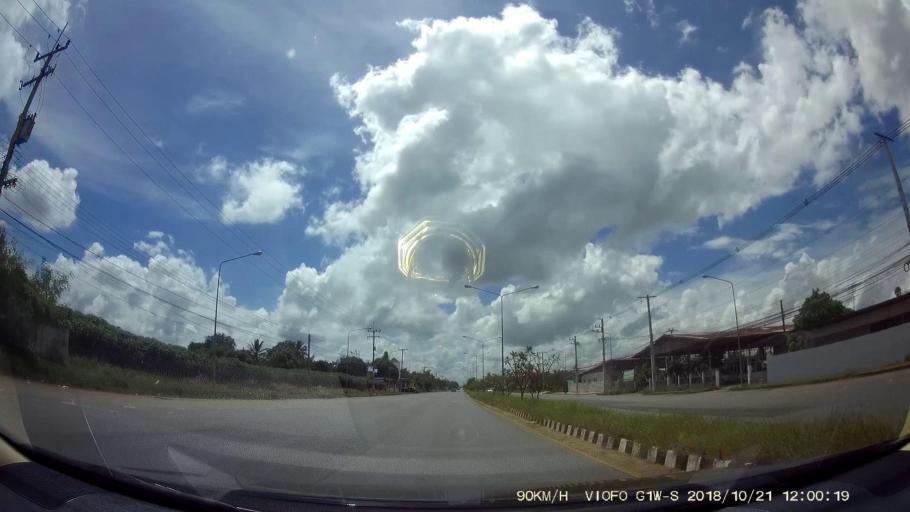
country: TH
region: Chaiyaphum
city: Chatturat
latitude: 15.5527
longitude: 101.8436
